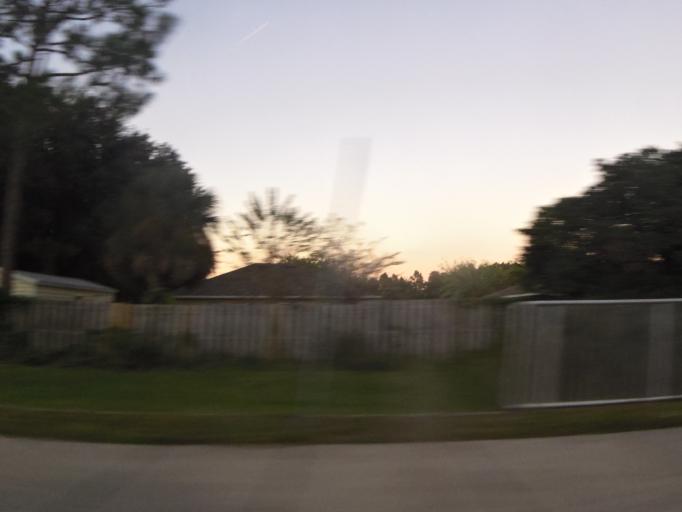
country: US
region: Florida
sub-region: Flagler County
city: Palm Coast
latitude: 29.5874
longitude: -81.2592
